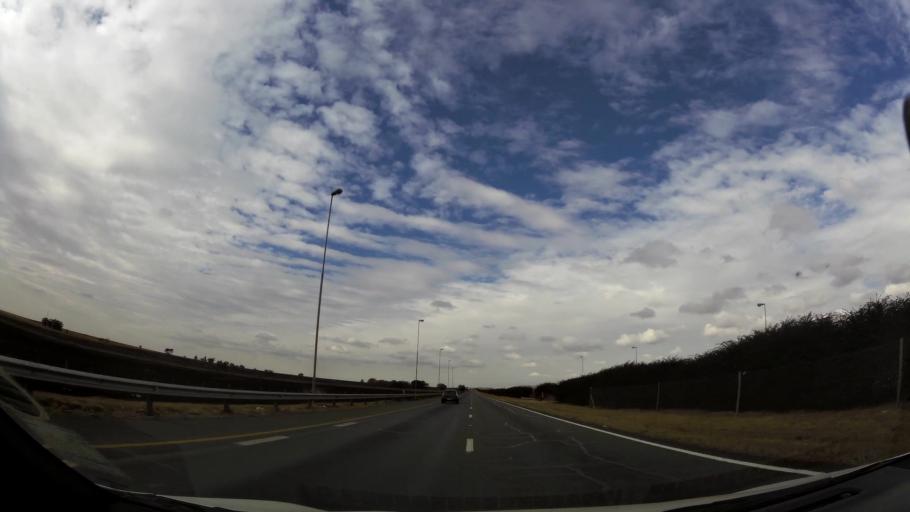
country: ZA
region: Gauteng
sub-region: Sedibeng District Municipality
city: Heidelberg
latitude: -26.3974
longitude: 28.2579
